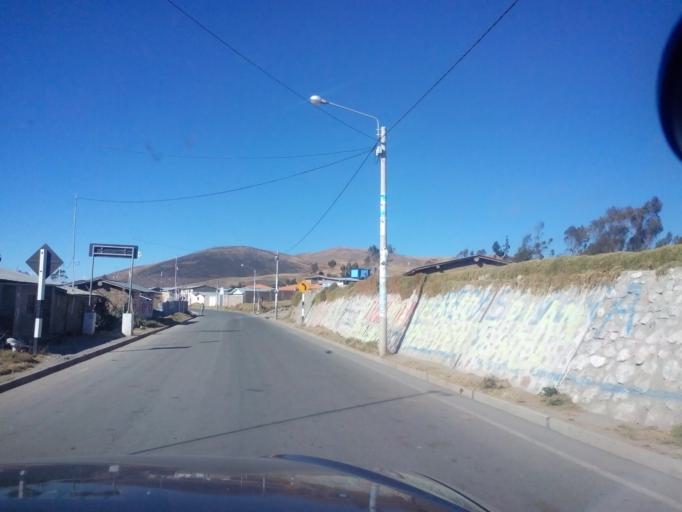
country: PE
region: Apurimac
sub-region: Provincia de Andahuaylas
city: Pacucha
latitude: -13.6510
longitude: -73.3000
